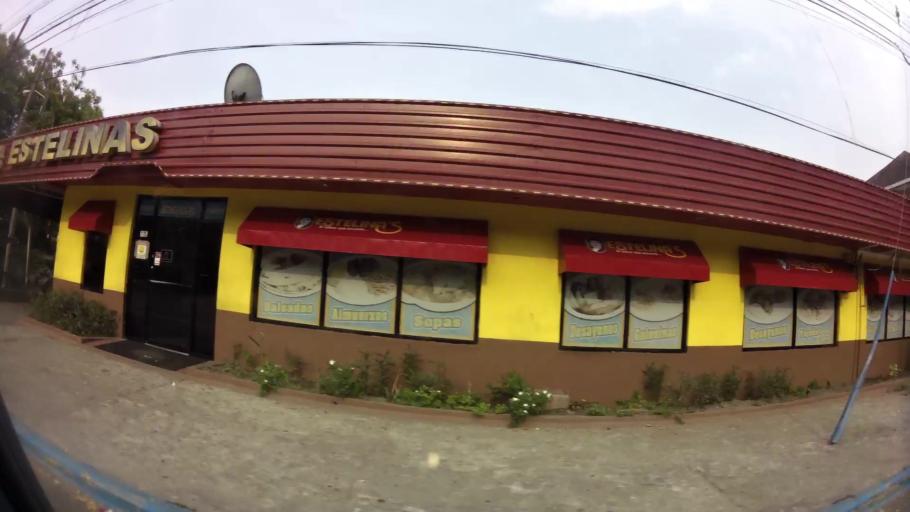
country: HN
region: Cortes
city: San Pedro Sula
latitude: 15.5145
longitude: -88.0310
